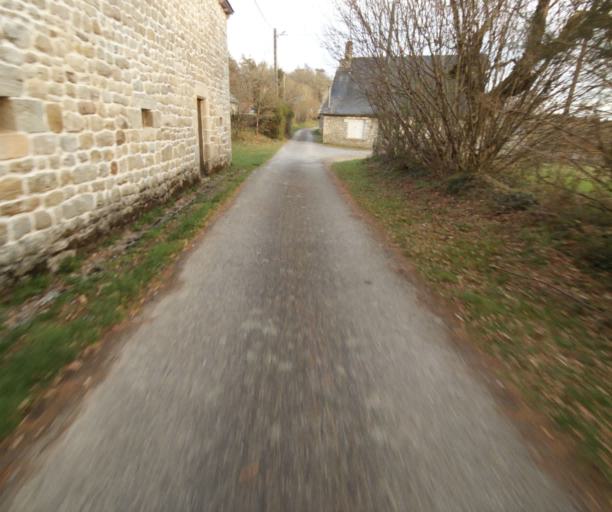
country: FR
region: Limousin
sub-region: Departement de la Correze
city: Argentat
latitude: 45.2476
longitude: 1.9637
